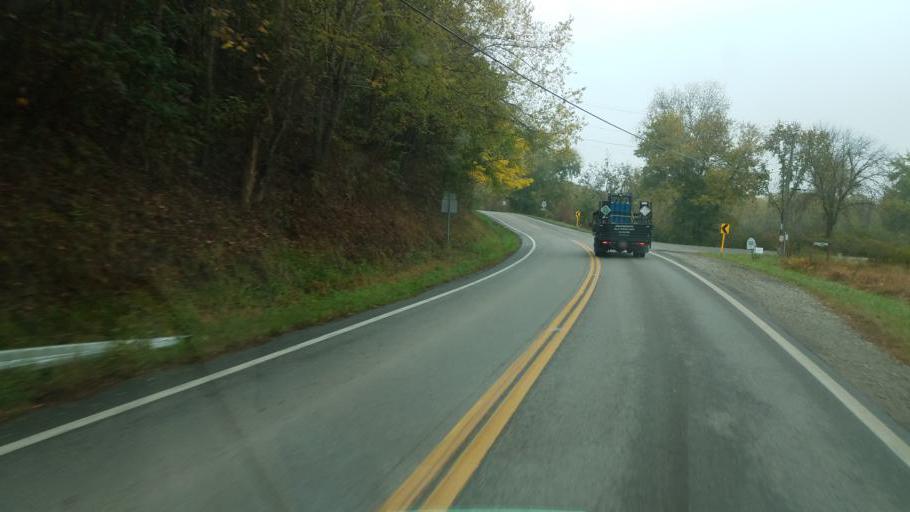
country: US
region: Ohio
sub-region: Carroll County
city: Carrollton
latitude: 40.4201
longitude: -81.1461
